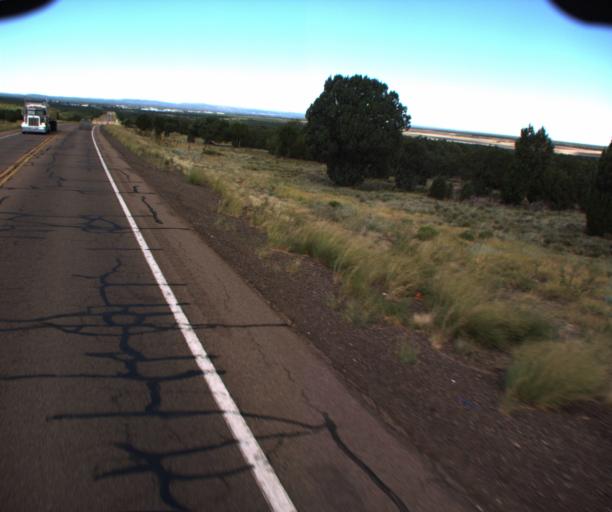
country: US
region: Arizona
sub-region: Navajo County
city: Show Low
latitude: 34.2639
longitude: -109.9635
